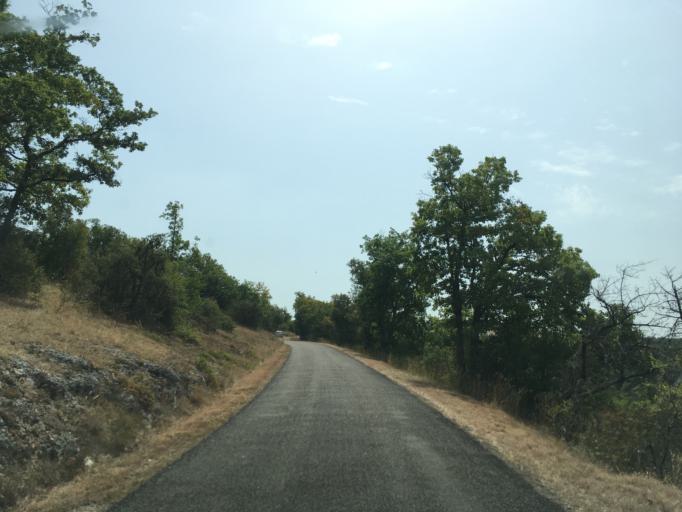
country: FR
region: Midi-Pyrenees
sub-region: Departement du Lot
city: Le Vigan
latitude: 44.7594
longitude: 1.5515
